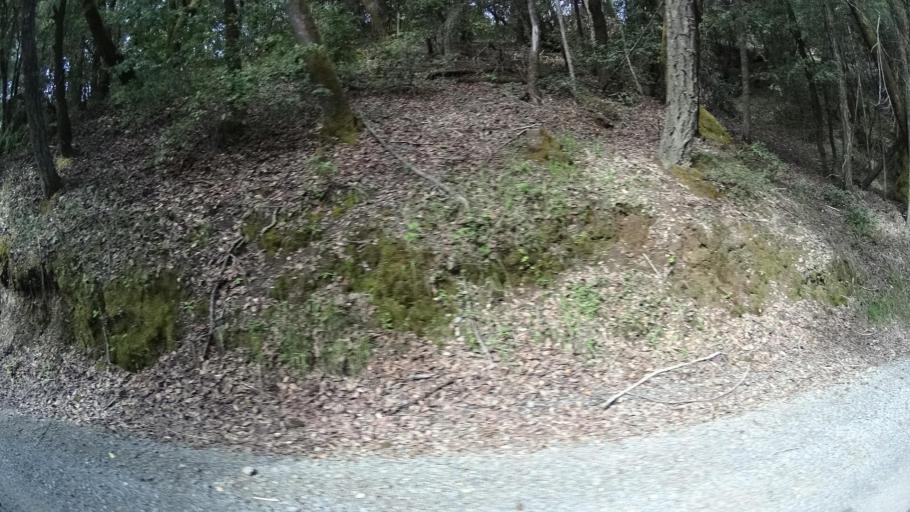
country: US
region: California
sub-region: Humboldt County
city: Redway
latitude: 40.0531
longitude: -123.8372
